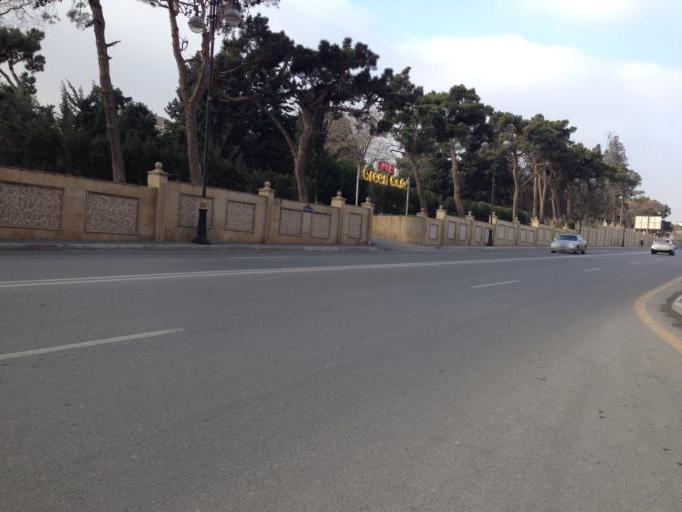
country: AZ
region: Baki
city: Baku
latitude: 40.3926
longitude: 49.8565
